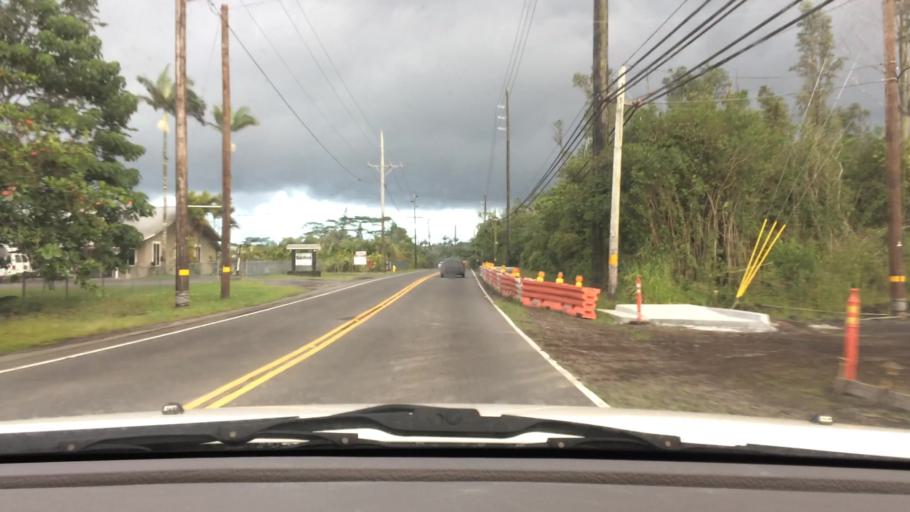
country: US
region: Hawaii
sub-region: Hawaii County
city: Hawaiian Paradise Park
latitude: 19.5023
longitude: -154.9551
